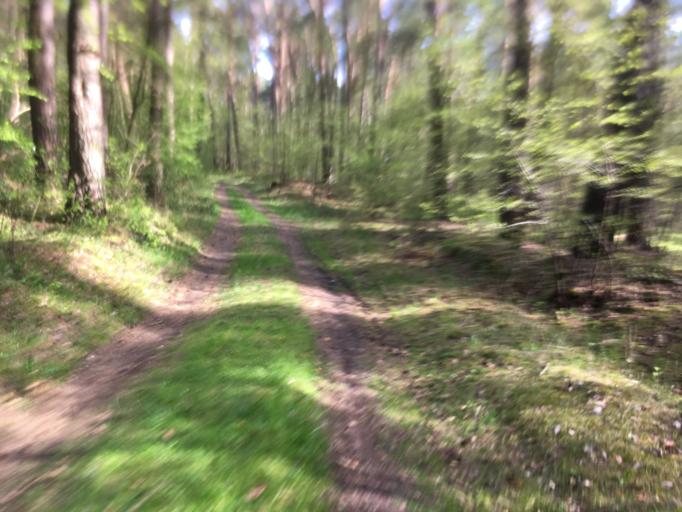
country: DE
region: Brandenburg
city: Bernau bei Berlin
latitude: 52.7101
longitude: 13.5709
